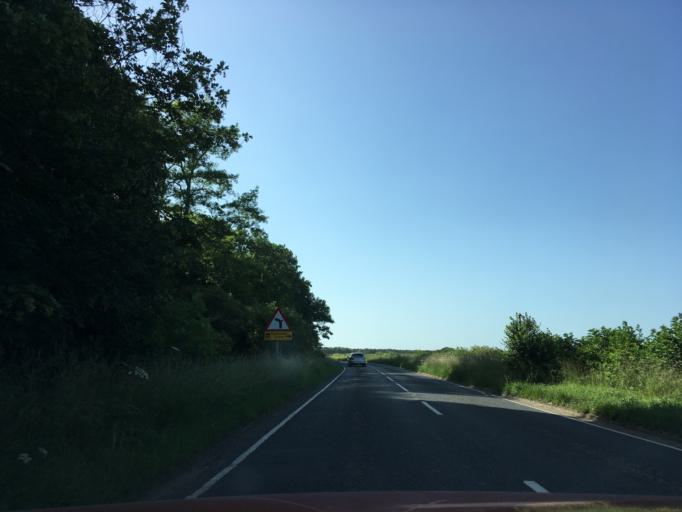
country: GB
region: England
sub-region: Oxfordshire
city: Somerton
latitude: 51.9146
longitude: -1.2365
